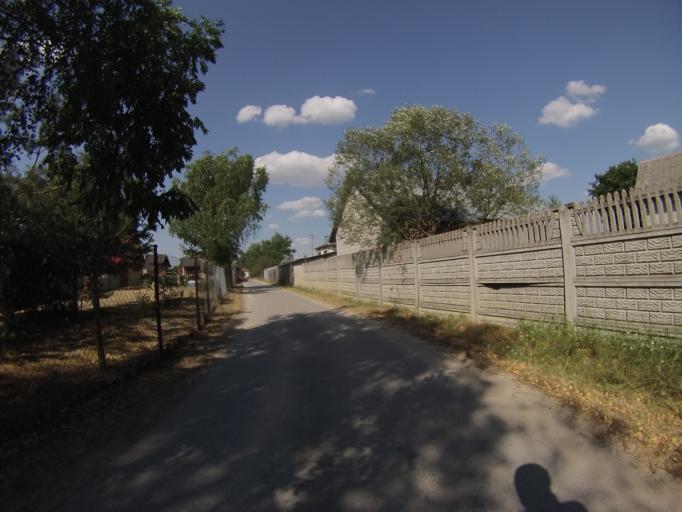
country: PL
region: Swietokrzyskie
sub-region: Powiat kielecki
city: Rakow
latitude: 50.6808
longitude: 21.0275
